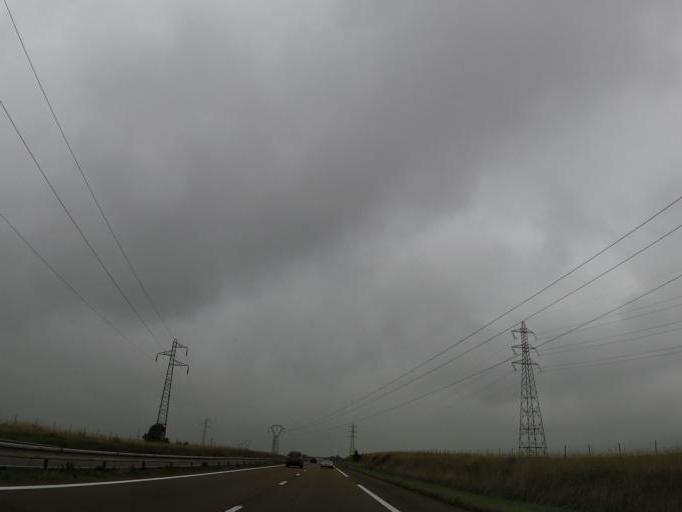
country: FR
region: Champagne-Ardenne
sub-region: Departement de la Marne
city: Sillery
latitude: 49.1831
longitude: 4.1505
